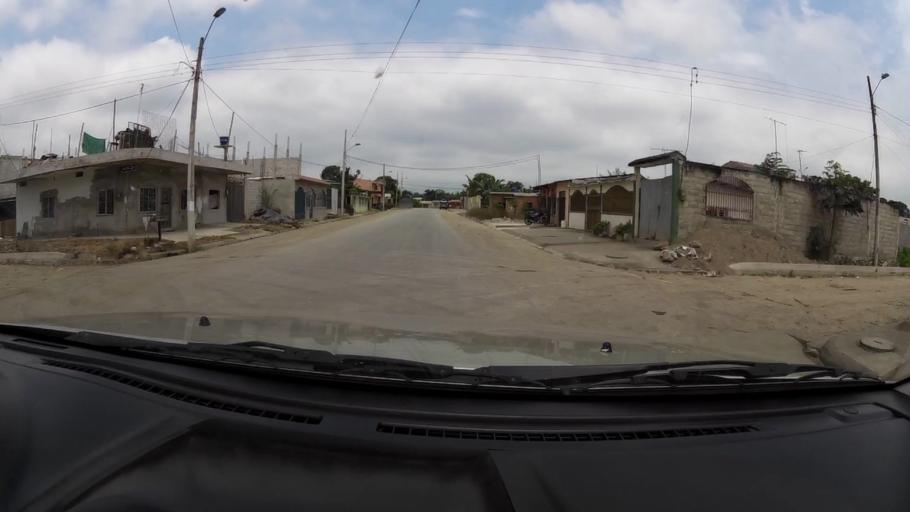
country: EC
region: El Oro
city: Pasaje
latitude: -3.2371
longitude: -79.8261
